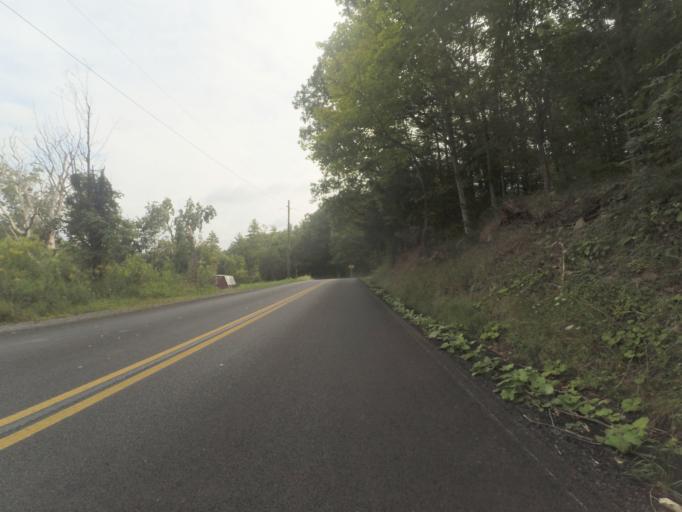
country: US
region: Pennsylvania
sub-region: Centre County
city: Milesburg
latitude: 41.0326
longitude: -77.7282
